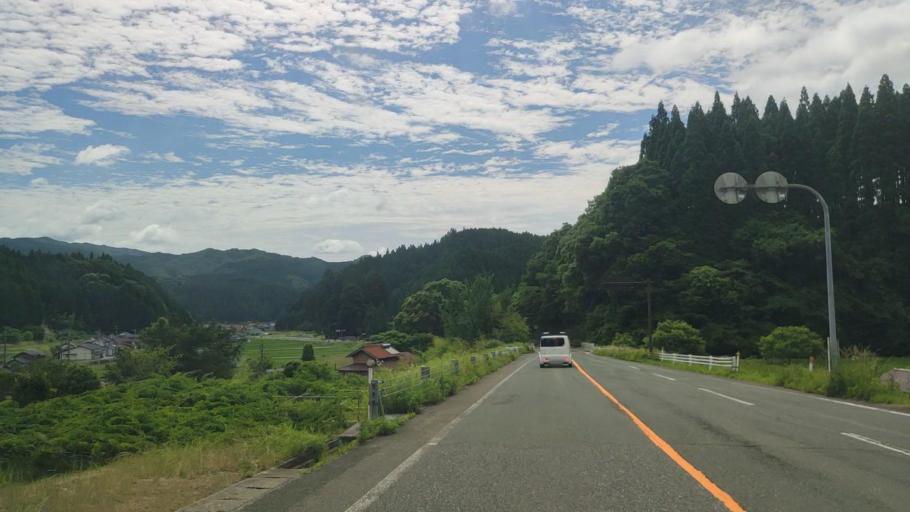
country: JP
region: Okayama
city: Niimi
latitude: 35.1787
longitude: 133.5574
